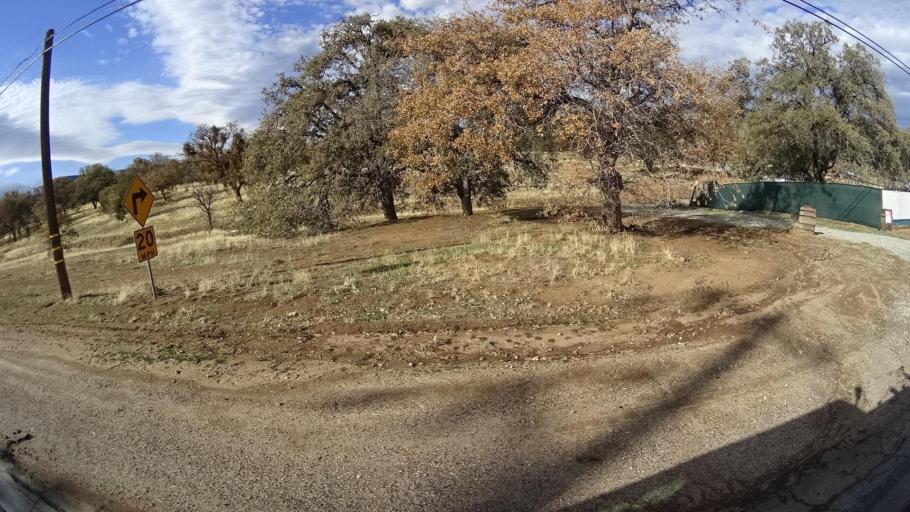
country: US
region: California
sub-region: Kern County
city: Golden Hills
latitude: 35.1182
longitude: -118.4950
